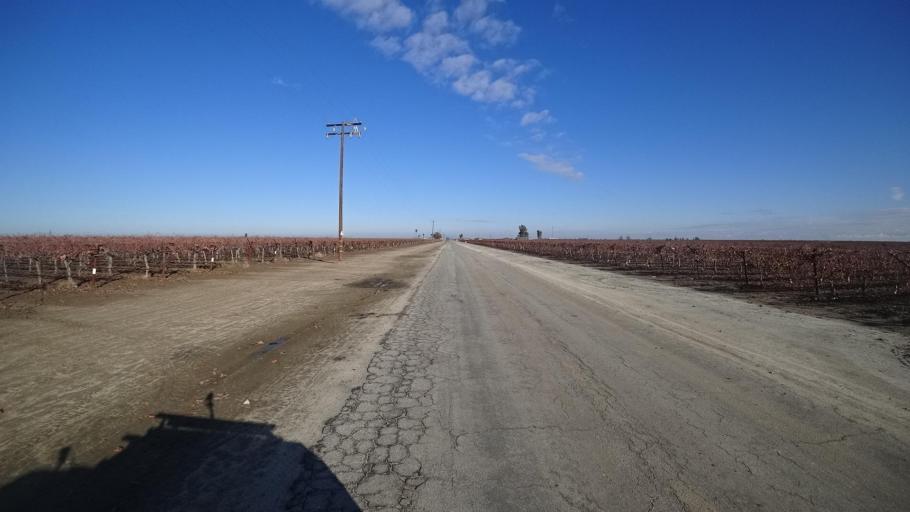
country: US
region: California
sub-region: Kern County
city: Delano
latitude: 35.7199
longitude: -119.2942
